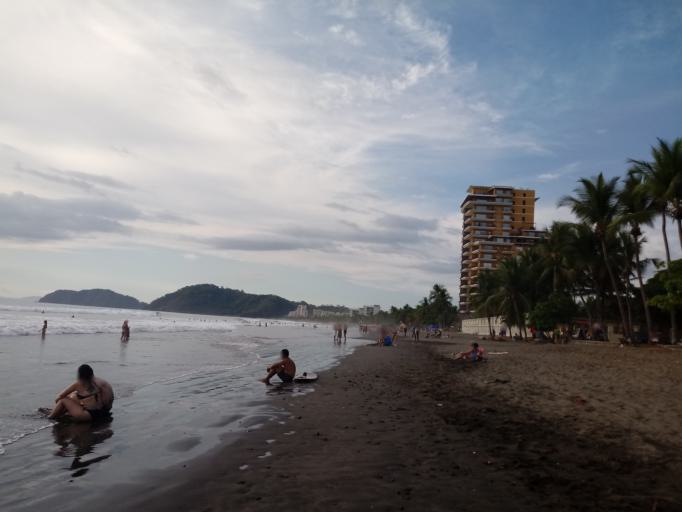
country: CR
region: Puntarenas
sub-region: Canton de Garabito
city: Jaco
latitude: 9.6087
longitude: -84.6259
